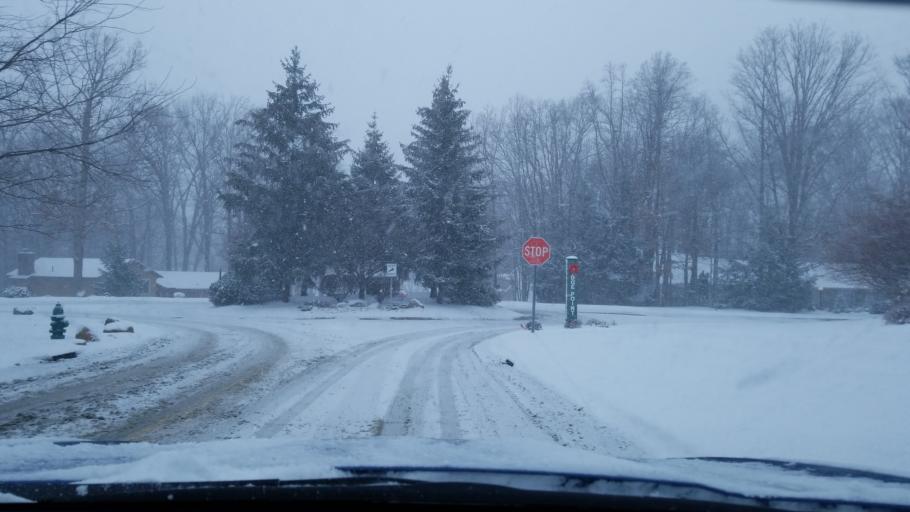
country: US
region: Ohio
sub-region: Cuyahoga County
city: Strongsville
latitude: 41.3206
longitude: -81.8209
